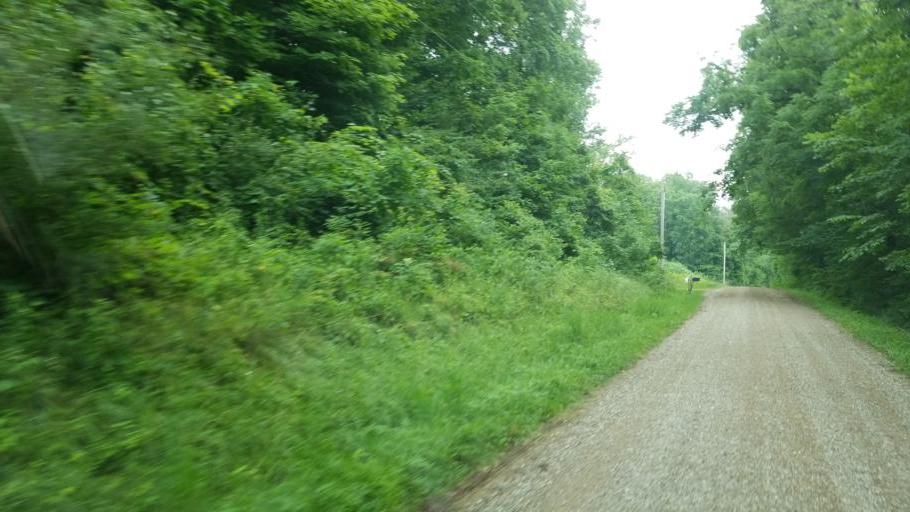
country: US
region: Ohio
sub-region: Knox County
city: Fredericktown
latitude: 40.4867
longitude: -82.6582
